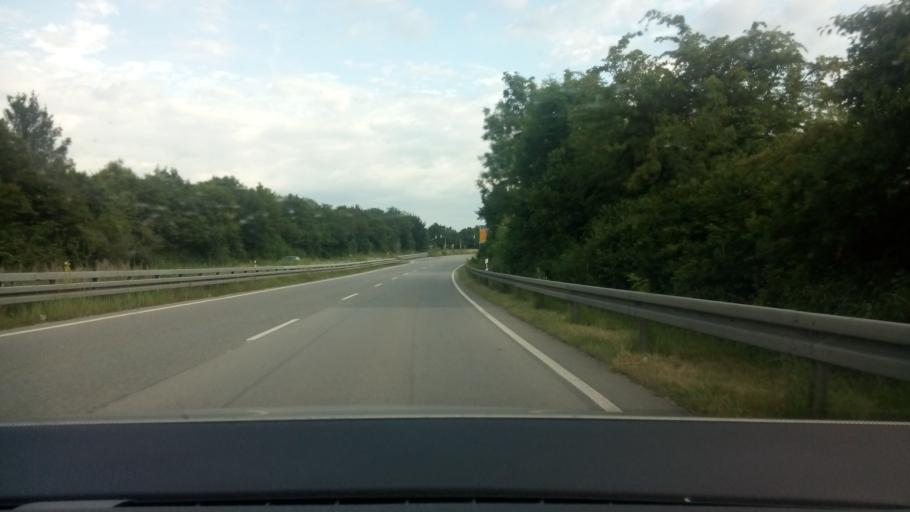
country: DE
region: Bavaria
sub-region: Upper Bavaria
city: Unterschleissheim
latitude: 48.2929
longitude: 11.5810
